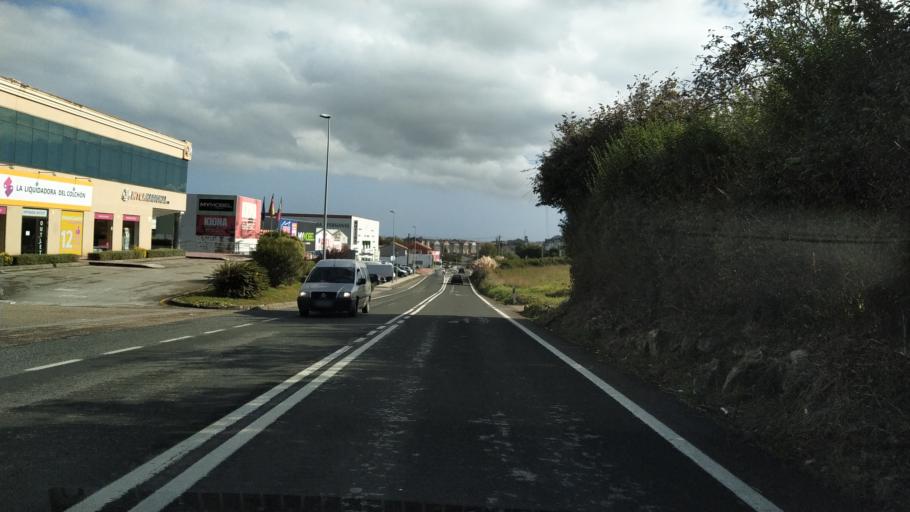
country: ES
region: Cantabria
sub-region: Provincia de Cantabria
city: Santa Cruz de Bezana
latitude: 43.4340
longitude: -3.9115
